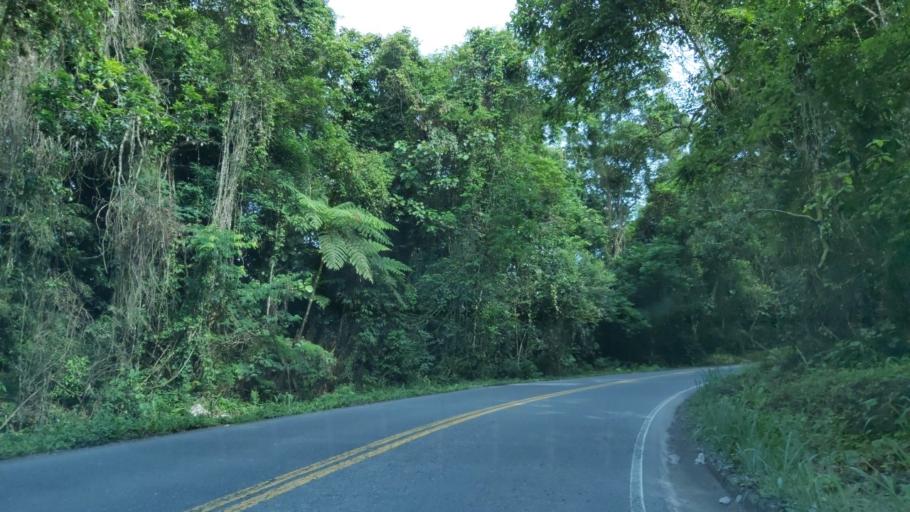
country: BR
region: Sao Paulo
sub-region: Juquia
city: Juquia
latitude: -24.1051
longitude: -47.6265
